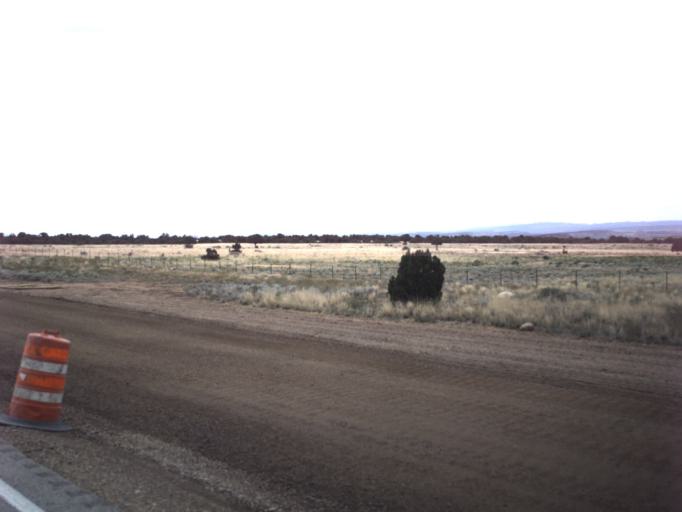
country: US
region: Utah
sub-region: Carbon County
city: East Carbon City
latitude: 39.4255
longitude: -110.4463
